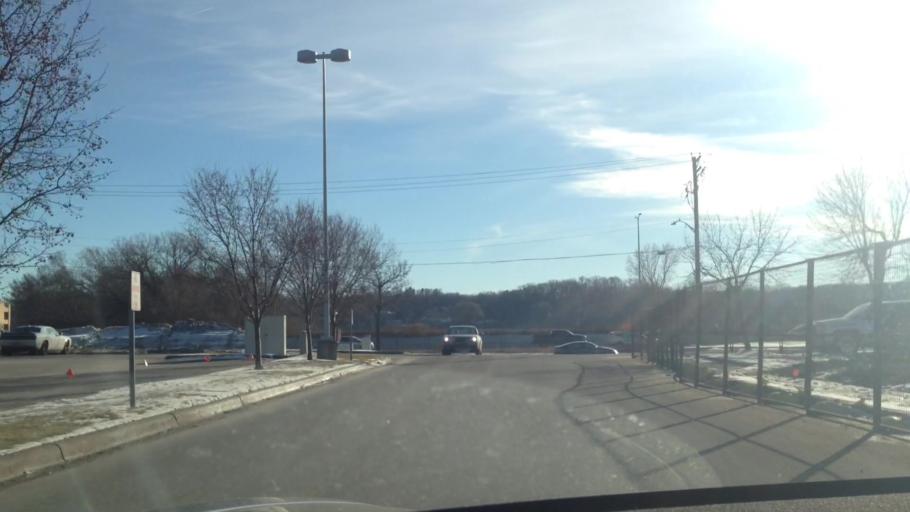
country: US
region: Minnesota
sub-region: Hennepin County
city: Minnetonka Mills
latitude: 44.9720
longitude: -93.4234
